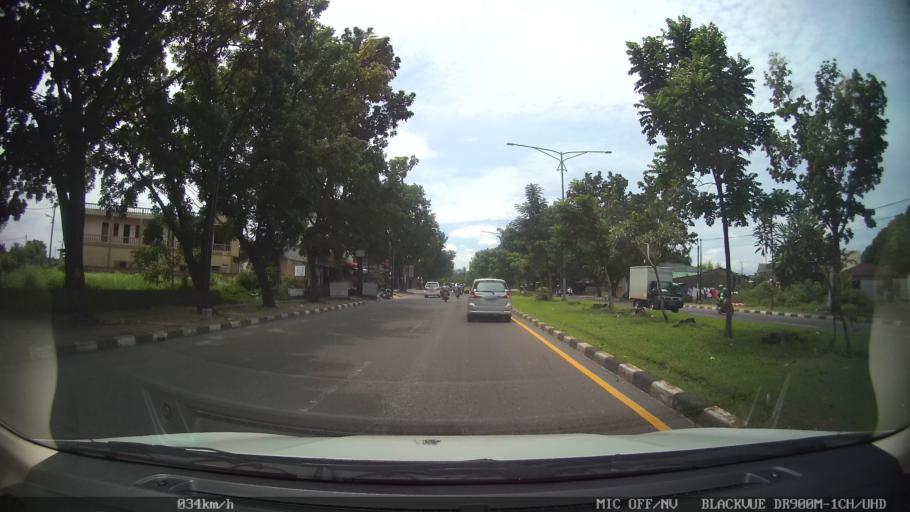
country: ID
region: North Sumatra
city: Sunggal
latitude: 3.5440
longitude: 98.6272
